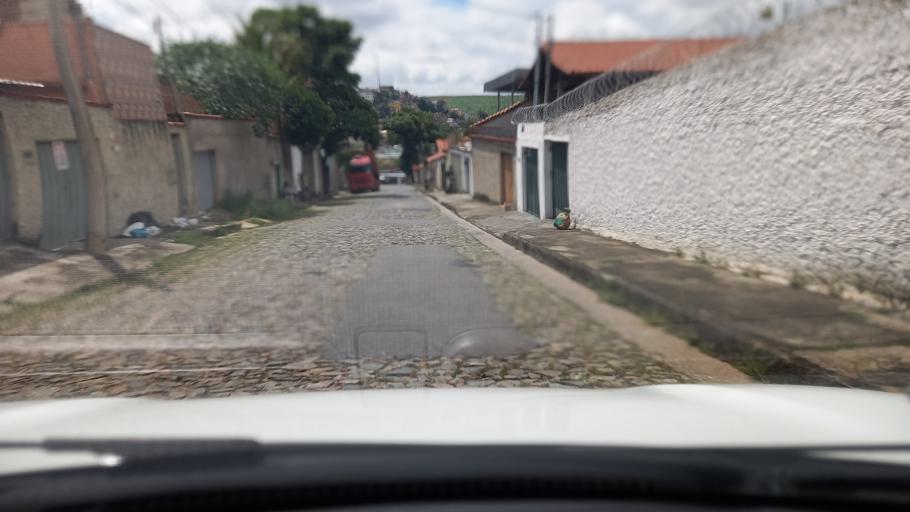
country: BR
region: Minas Gerais
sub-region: Contagem
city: Contagem
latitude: -19.9008
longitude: -44.0211
